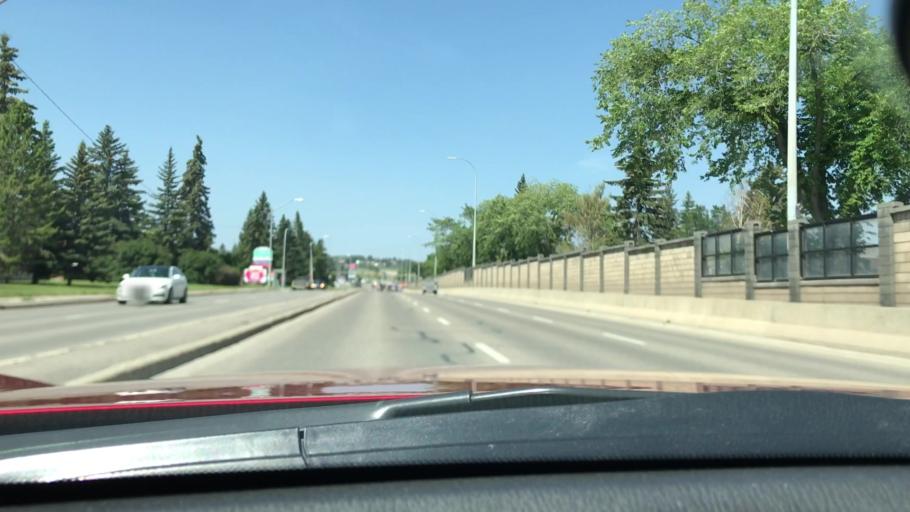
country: CA
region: Alberta
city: Calgary
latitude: 51.0471
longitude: -114.1475
